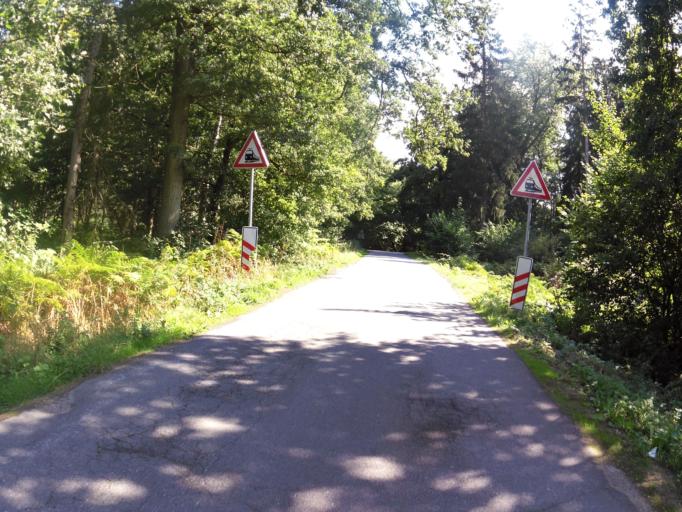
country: DE
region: North Rhine-Westphalia
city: Stolberg
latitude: 50.7925
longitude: 6.1992
